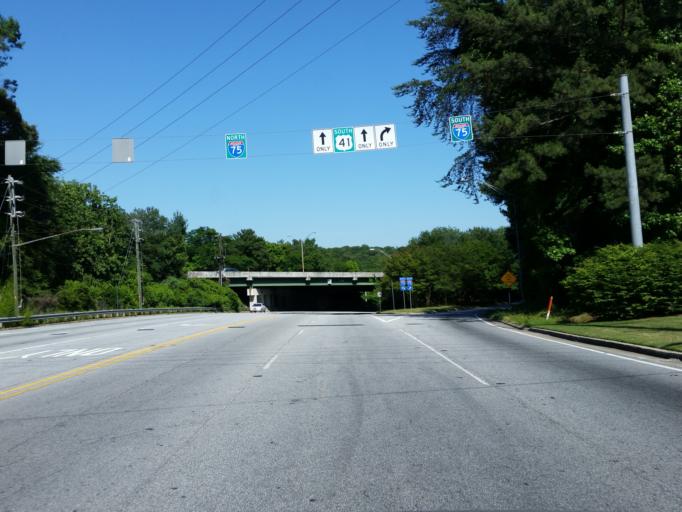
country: US
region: Georgia
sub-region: Cobb County
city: Vinings
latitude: 33.8633
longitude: -84.4399
